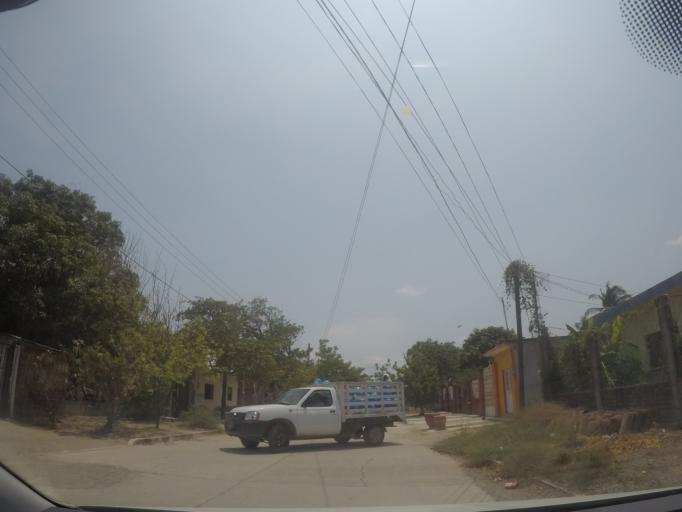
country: MX
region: Oaxaca
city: Asuncion Ixtaltepec
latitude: 16.5072
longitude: -95.0658
